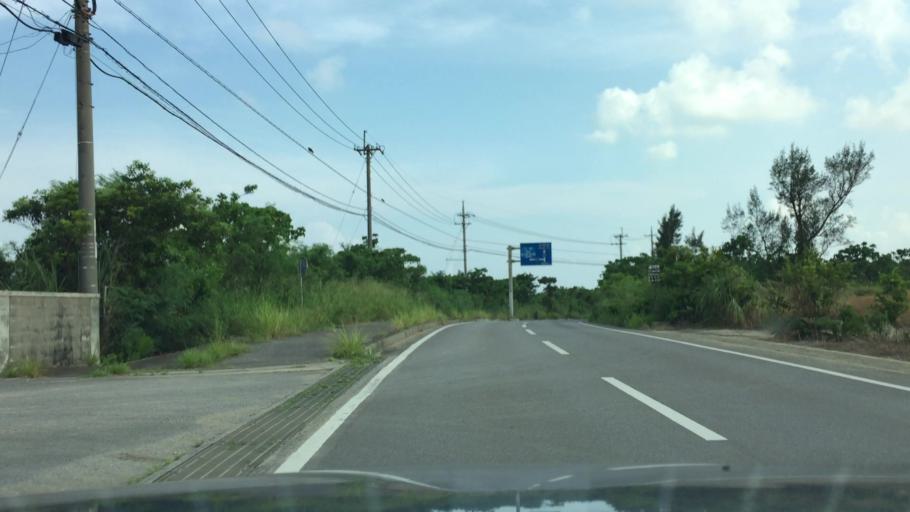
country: JP
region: Okinawa
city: Ishigaki
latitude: 24.3952
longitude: 124.1954
